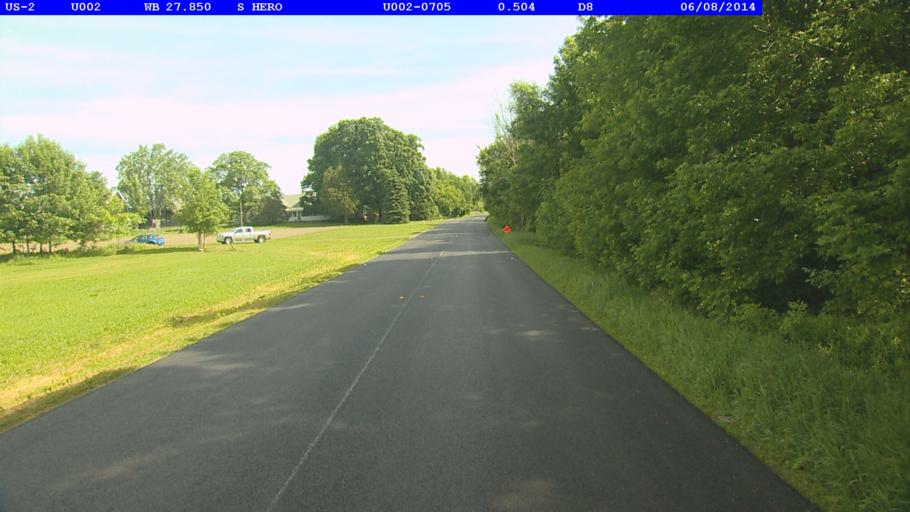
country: US
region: New York
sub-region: Clinton County
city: Cumberland Head
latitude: 44.6736
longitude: -73.3203
